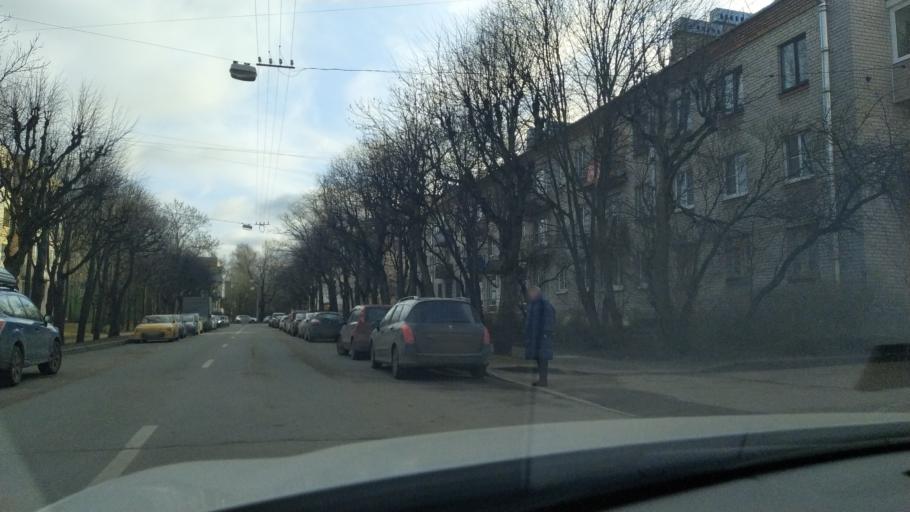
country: RU
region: St.-Petersburg
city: Pushkin
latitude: 59.7199
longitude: 30.4168
